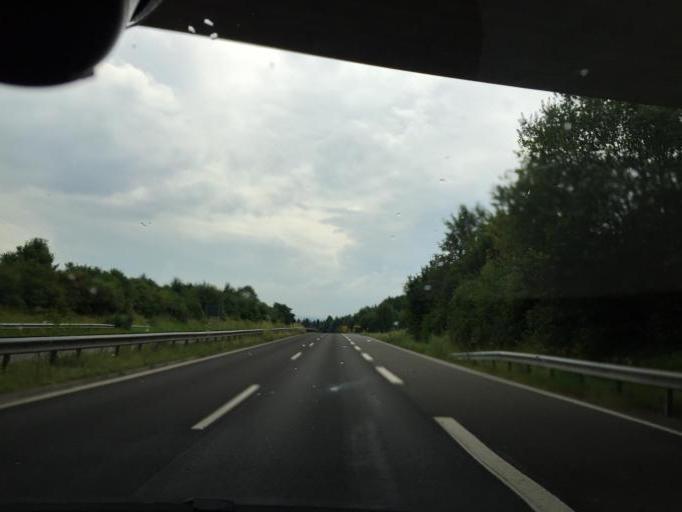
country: DE
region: Rheinland-Pfalz
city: Melsbach
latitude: 50.4761
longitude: 7.4877
